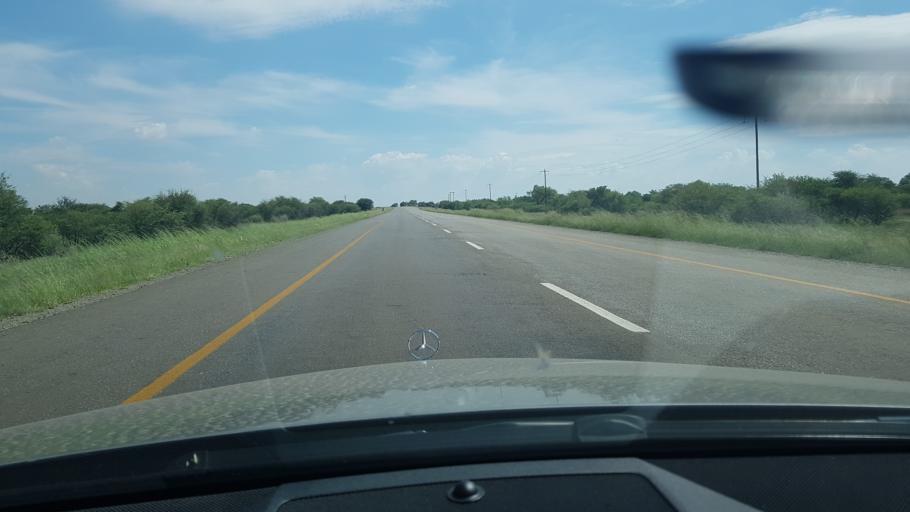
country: ZA
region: North-West
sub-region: Dr Kenneth Kaunda District Municipality
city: Wolmaransstad
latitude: -27.2493
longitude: 25.9470
